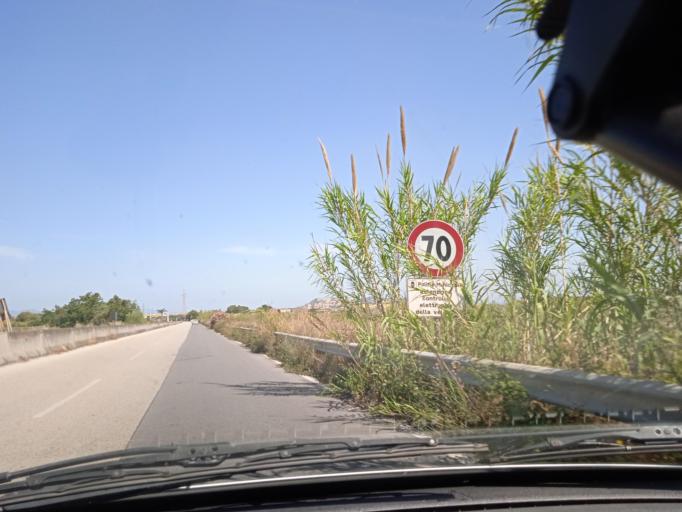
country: IT
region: Sicily
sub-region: Messina
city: San Filippo del Mela
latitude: 38.1895
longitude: 15.2616
